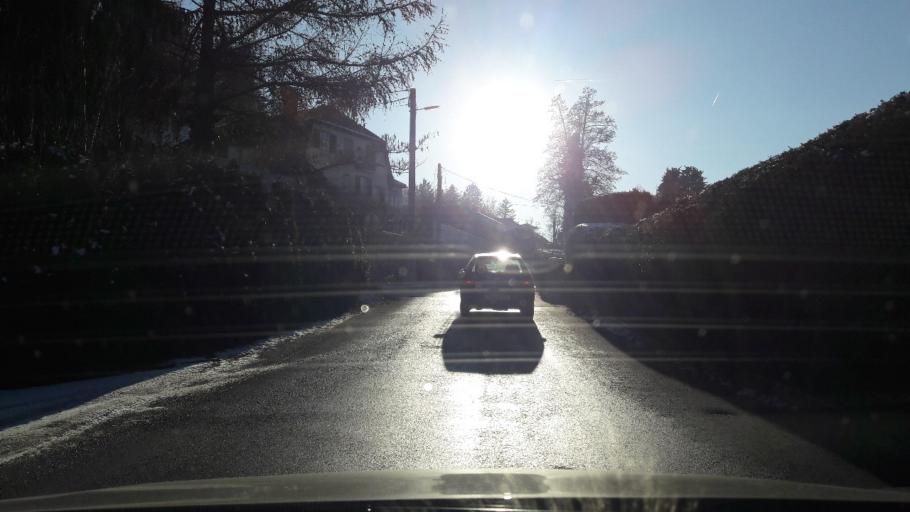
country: AT
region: Styria
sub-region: Graz Stadt
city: Mariatrost
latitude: 47.0992
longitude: 15.4788
